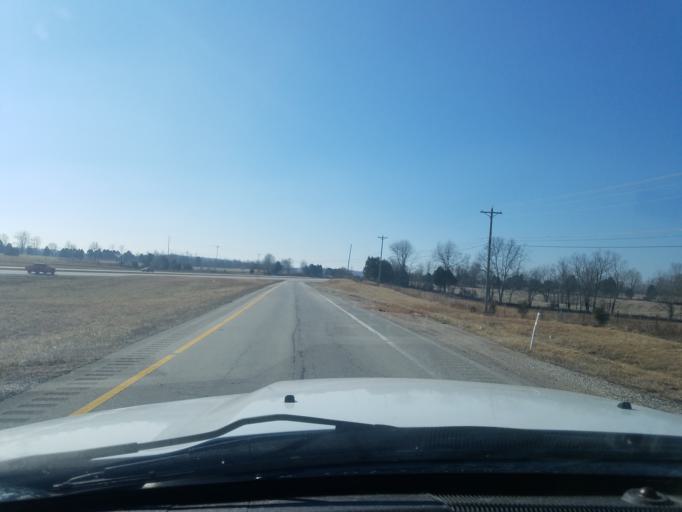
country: US
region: Kentucky
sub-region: Hardin County
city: Elizabethtown
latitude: 37.5717
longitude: -86.0392
